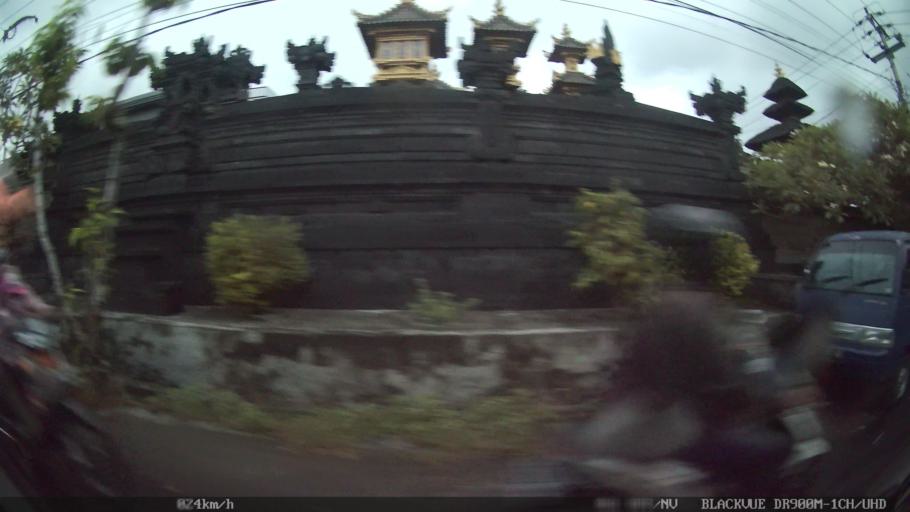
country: ID
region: Bali
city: Banjar Pasekan
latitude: -8.6176
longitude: 115.2728
